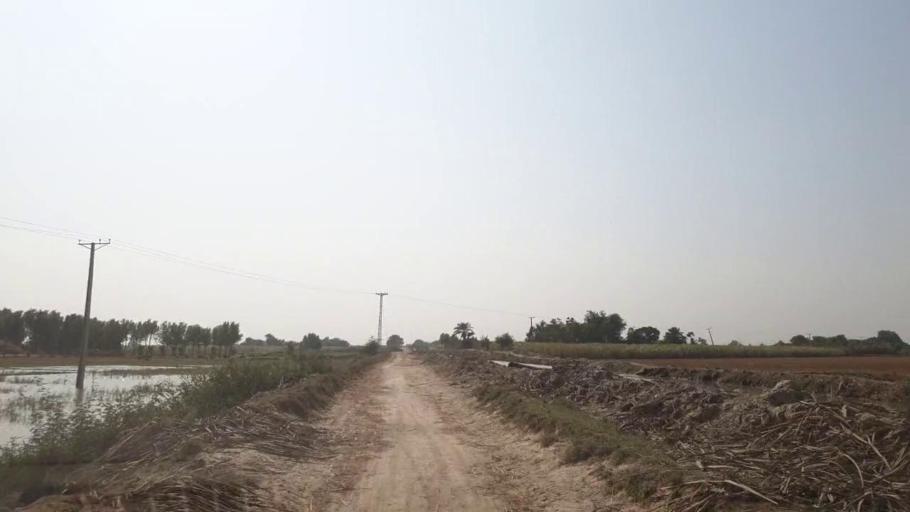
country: PK
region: Sindh
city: Bulri
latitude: 24.9616
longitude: 68.3900
